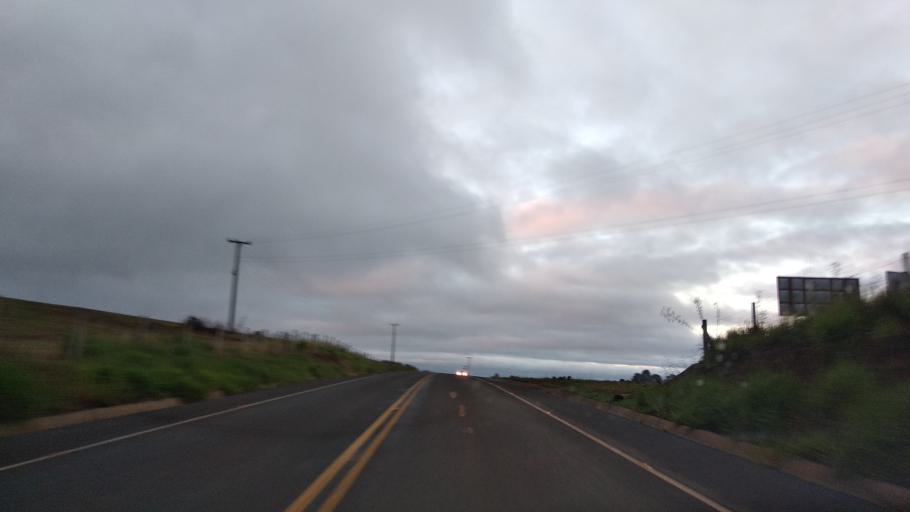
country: BR
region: Santa Catarina
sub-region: Campos Novos
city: Campos Novos
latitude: -27.3700
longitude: -51.2036
